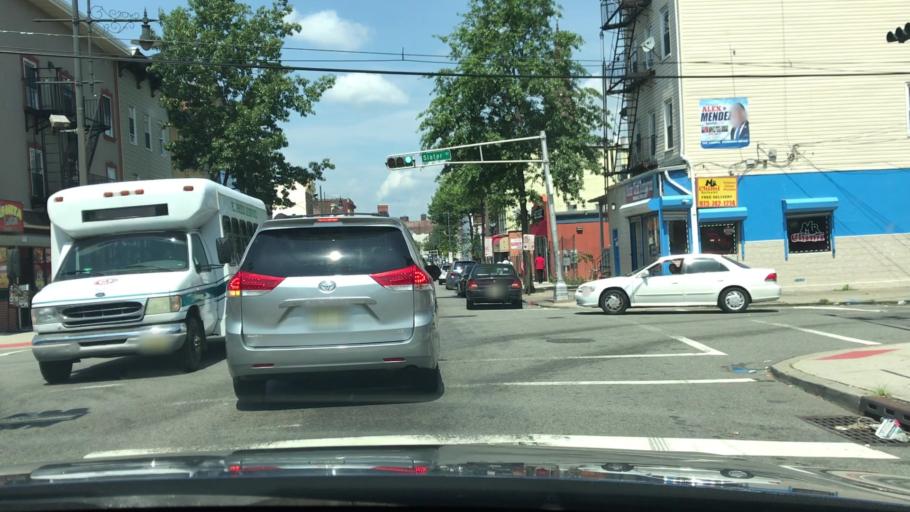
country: US
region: New Jersey
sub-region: Passaic County
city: Paterson
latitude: 40.9106
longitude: -74.1719
